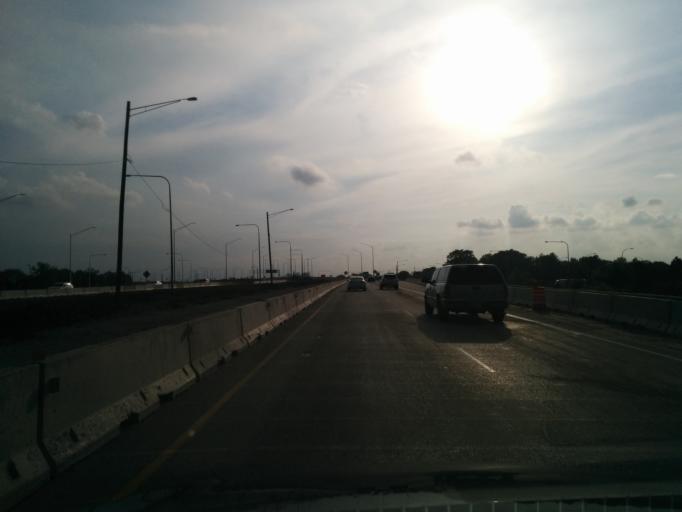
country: US
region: Illinois
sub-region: DuPage County
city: Roselle
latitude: 41.9972
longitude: -88.1104
